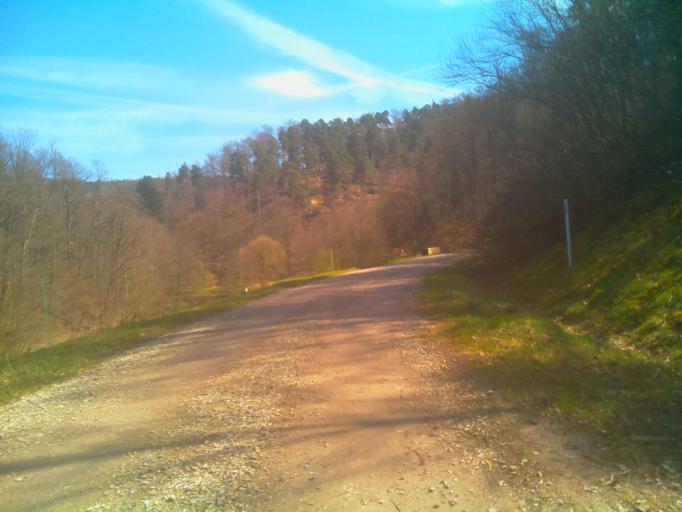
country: DE
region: Baden-Wuerttemberg
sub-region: Karlsruhe Region
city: Wilhelmsfeld
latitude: 49.4752
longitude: 8.7210
